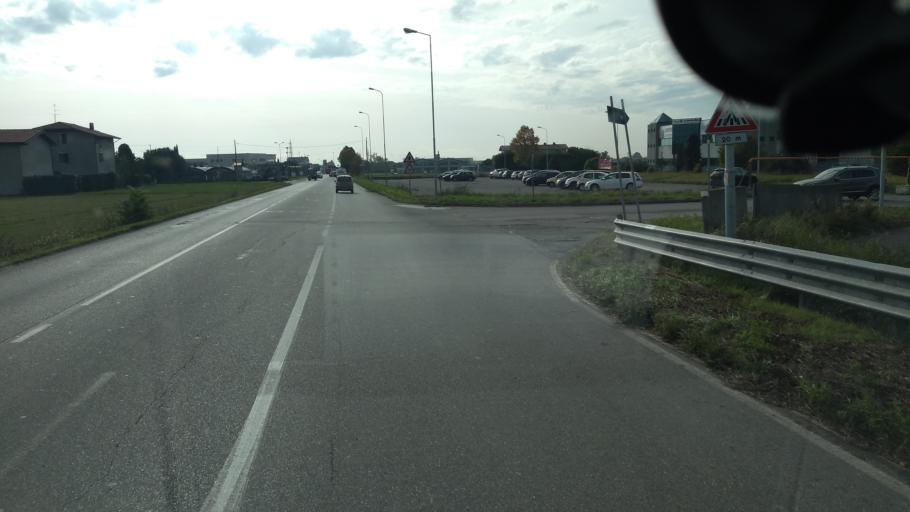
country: IT
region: Lombardy
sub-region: Provincia di Bergamo
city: Zanica
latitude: 45.6245
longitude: 9.6897
